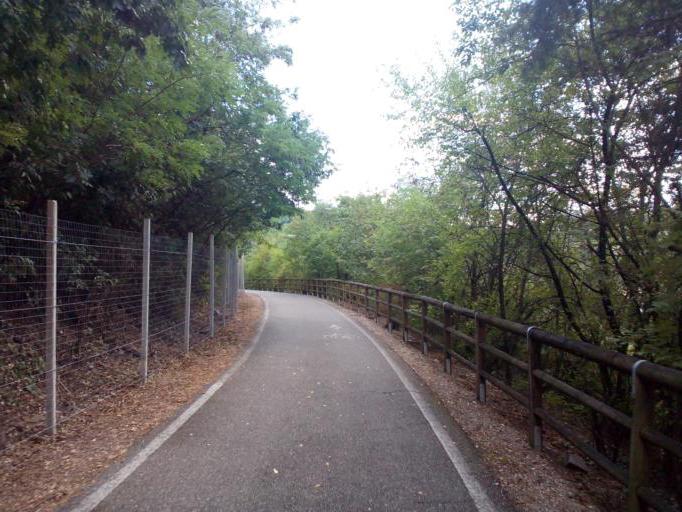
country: IT
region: Trentino-Alto Adige
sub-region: Bolzano
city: Cornaiano
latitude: 46.4815
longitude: 11.2986
